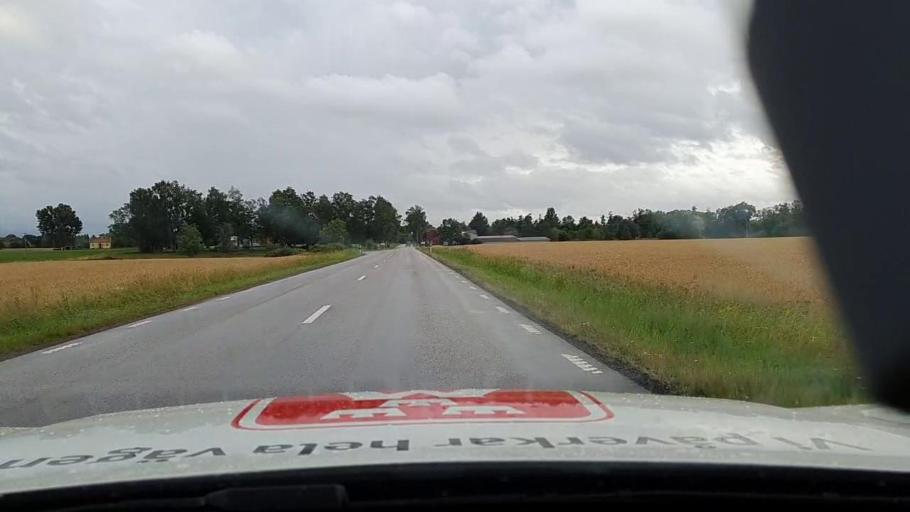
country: SE
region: Vaestra Goetaland
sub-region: Toreboda Kommun
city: Toereboda
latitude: 58.5845
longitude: 14.0058
